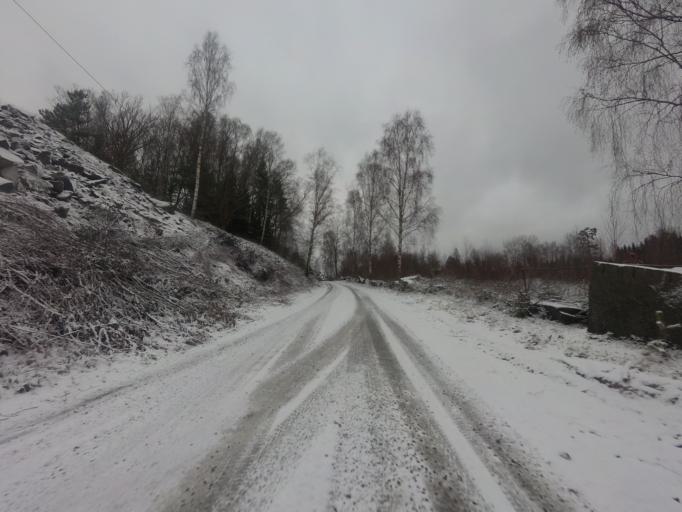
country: SE
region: Skane
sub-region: Osby Kommun
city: Lonsboda
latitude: 56.3957
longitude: 14.2499
